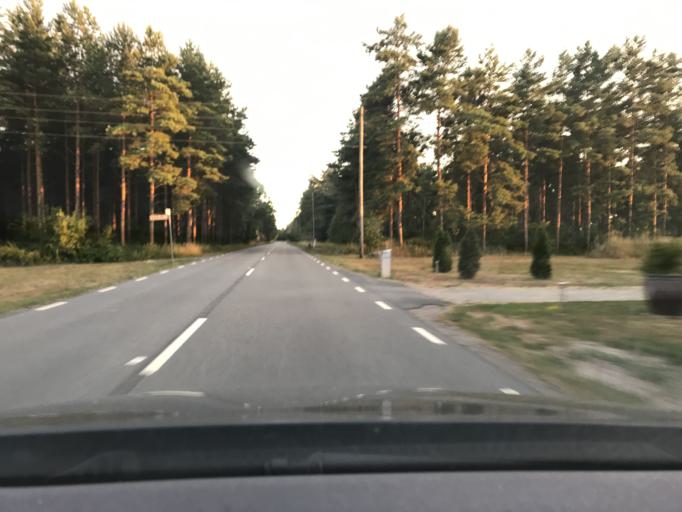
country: SE
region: Skane
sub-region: Simrishamns Kommun
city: Simrishamn
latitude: 55.4013
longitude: 14.1831
